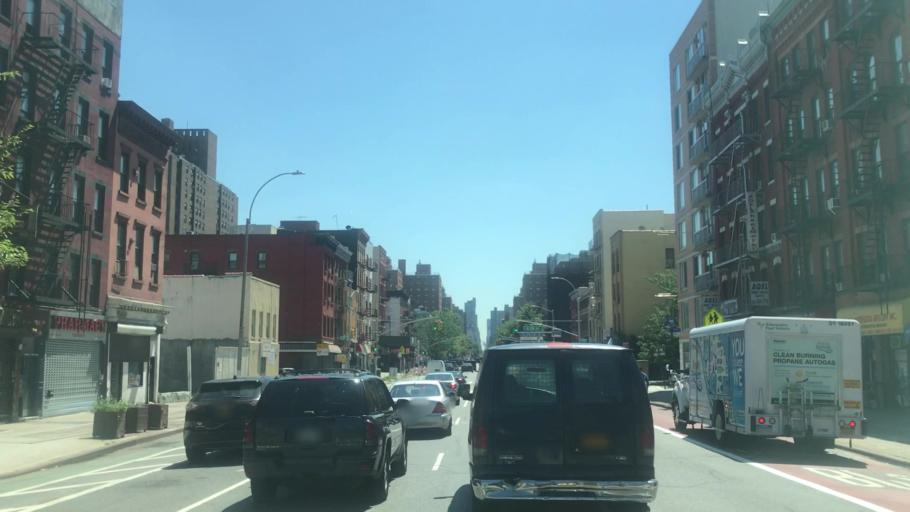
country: US
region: New York
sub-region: New York County
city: Manhattan
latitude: 40.7990
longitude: -73.9364
